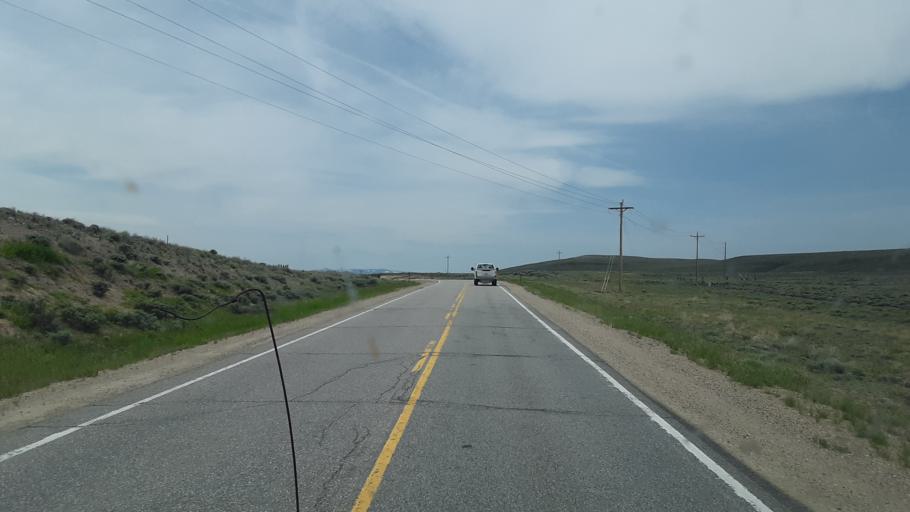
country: US
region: Colorado
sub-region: Jackson County
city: Walden
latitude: 40.6628
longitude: -106.3944
